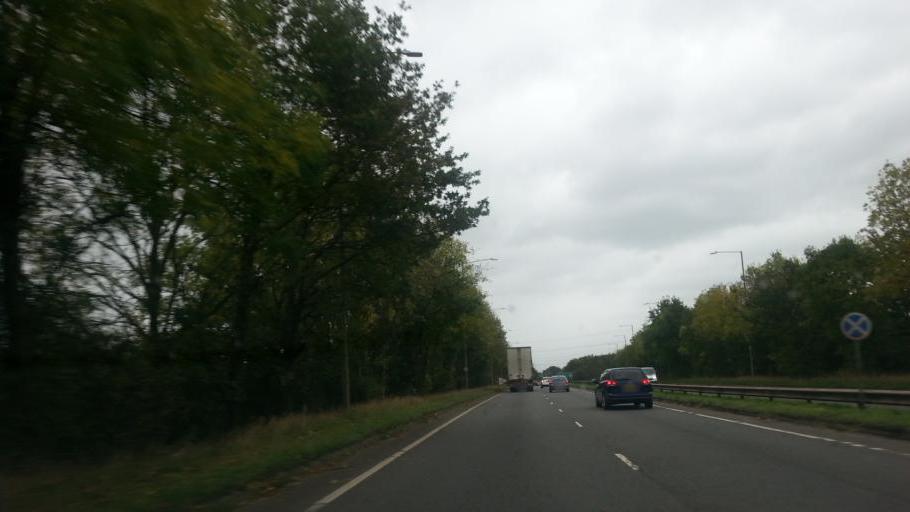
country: GB
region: England
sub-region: Warwickshire
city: Exhall
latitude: 52.4565
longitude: -1.4988
